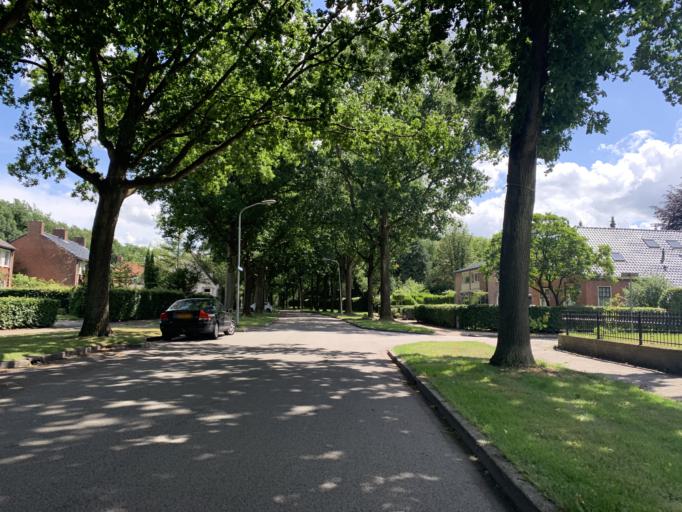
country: NL
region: Groningen
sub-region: Gemeente Haren
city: Haren
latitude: 53.1647
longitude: 6.6155
